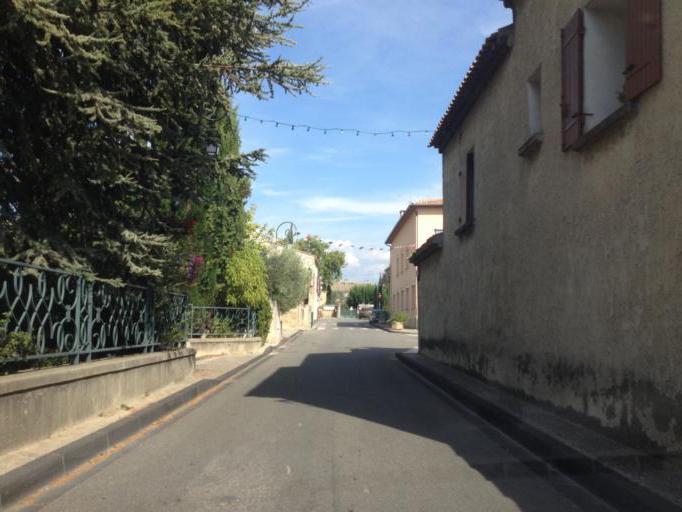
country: FR
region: Provence-Alpes-Cote d'Azur
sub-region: Departement du Vaucluse
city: Vacqueyras
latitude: 44.1380
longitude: 4.9838
